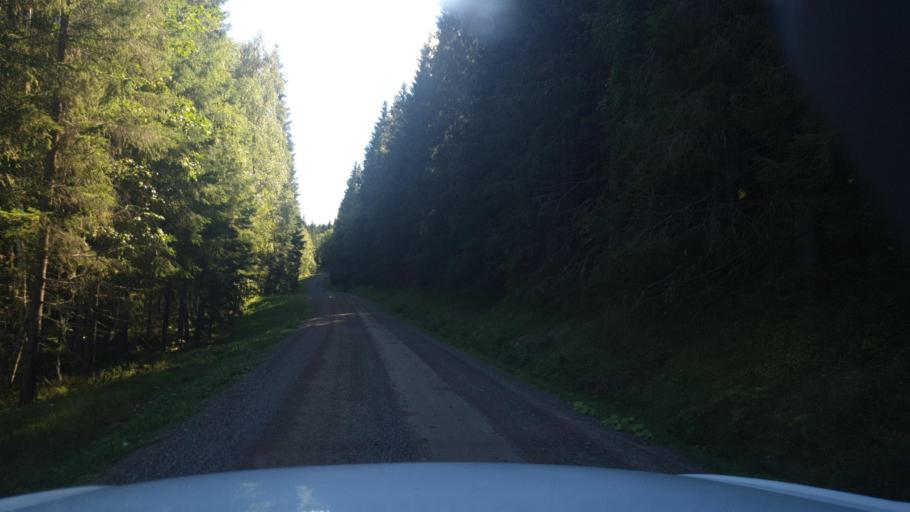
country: SE
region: Vaermland
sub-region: Eda Kommun
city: Charlottenberg
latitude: 60.0665
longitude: 12.5384
